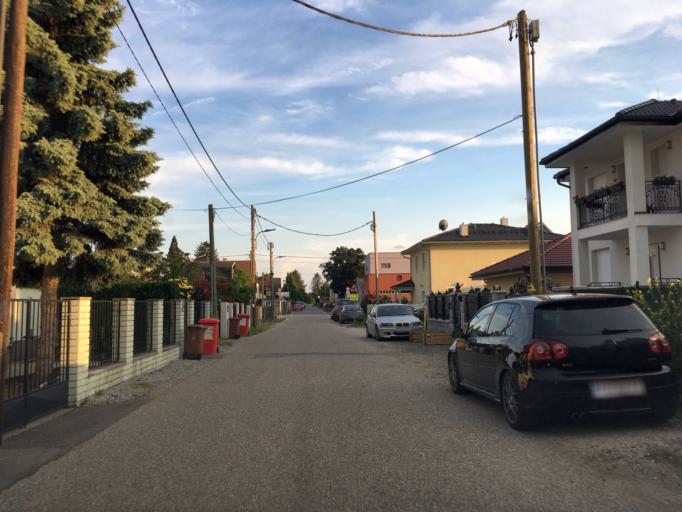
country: AT
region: Lower Austria
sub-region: Politischer Bezirk Wien-Umgebung
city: Gerasdorf bei Wien
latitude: 48.3141
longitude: 16.4968
